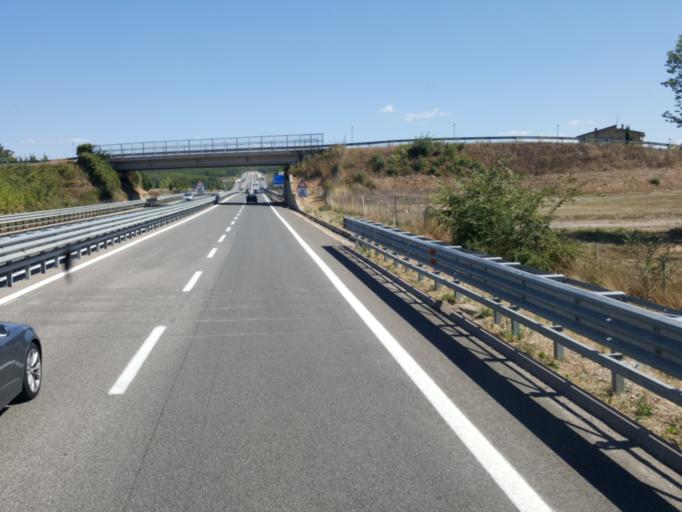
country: IT
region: Tuscany
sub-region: Provincia di Grosseto
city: Campagnatico
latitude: 42.9331
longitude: 11.2672
